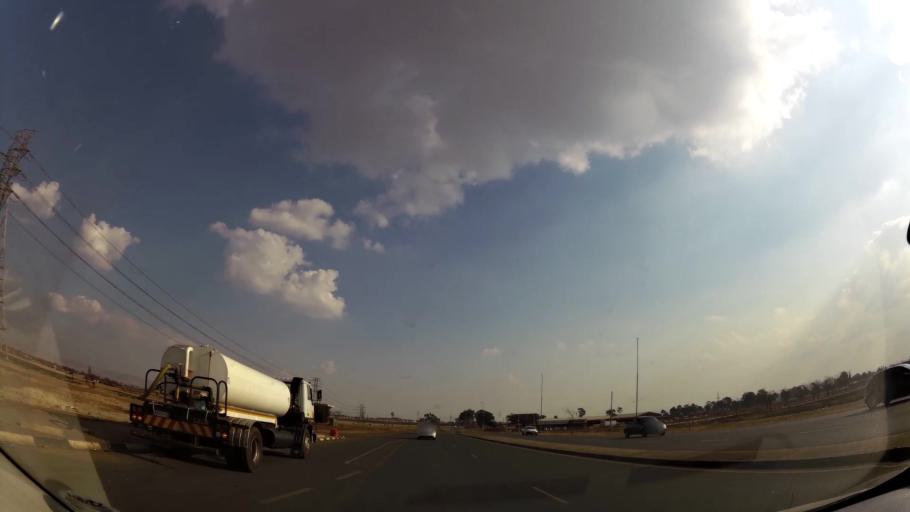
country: ZA
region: Gauteng
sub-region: Ekurhuleni Metropolitan Municipality
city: Germiston
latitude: -26.3345
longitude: 28.2317
